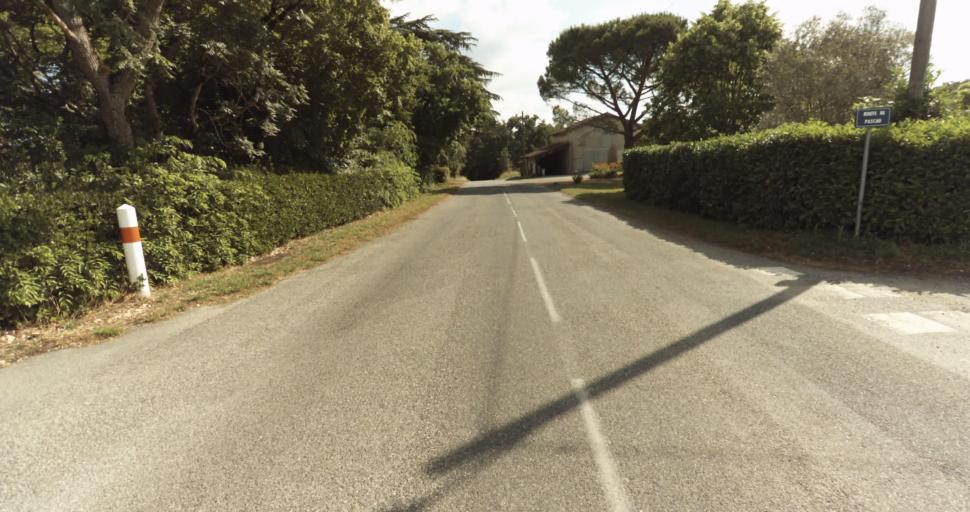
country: FR
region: Midi-Pyrenees
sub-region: Departement de la Haute-Garonne
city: Fonsorbes
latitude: 43.5609
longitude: 1.2317
